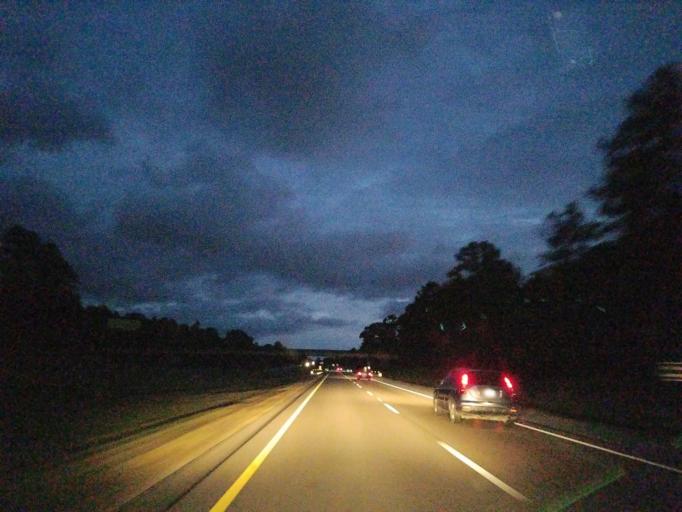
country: US
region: Mississippi
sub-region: Jones County
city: Sharon
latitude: 31.8150
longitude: -89.0527
